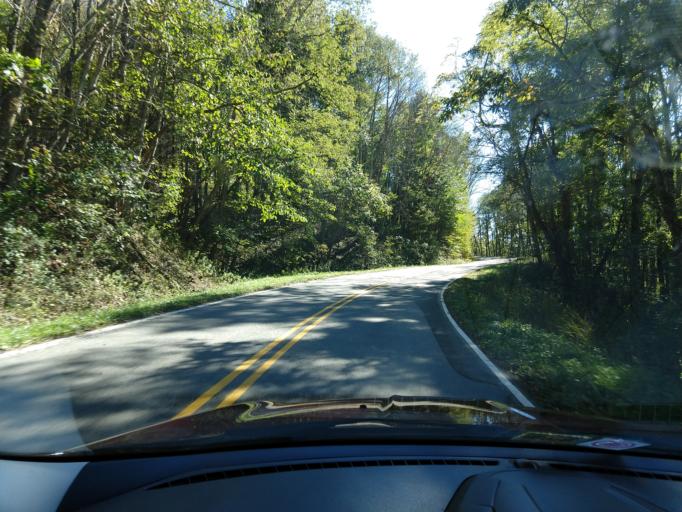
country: US
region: Virginia
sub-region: Alleghany County
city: Clifton Forge
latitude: 37.8818
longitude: -79.8879
